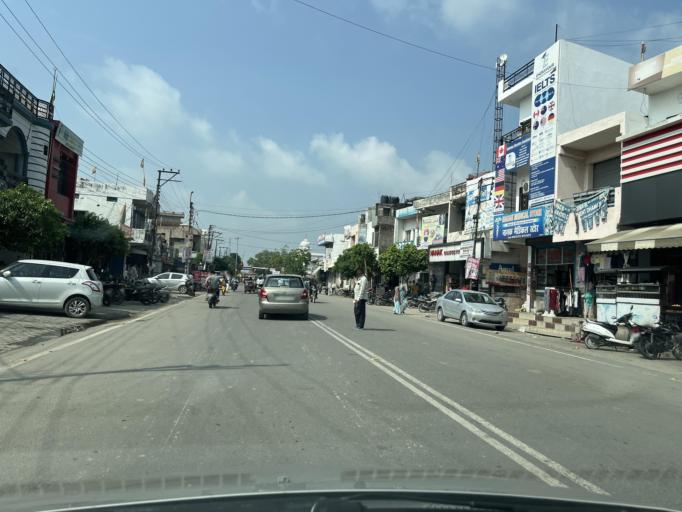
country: IN
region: Uttarakhand
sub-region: Udham Singh Nagar
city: Bazpur
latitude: 29.1589
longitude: 79.1512
